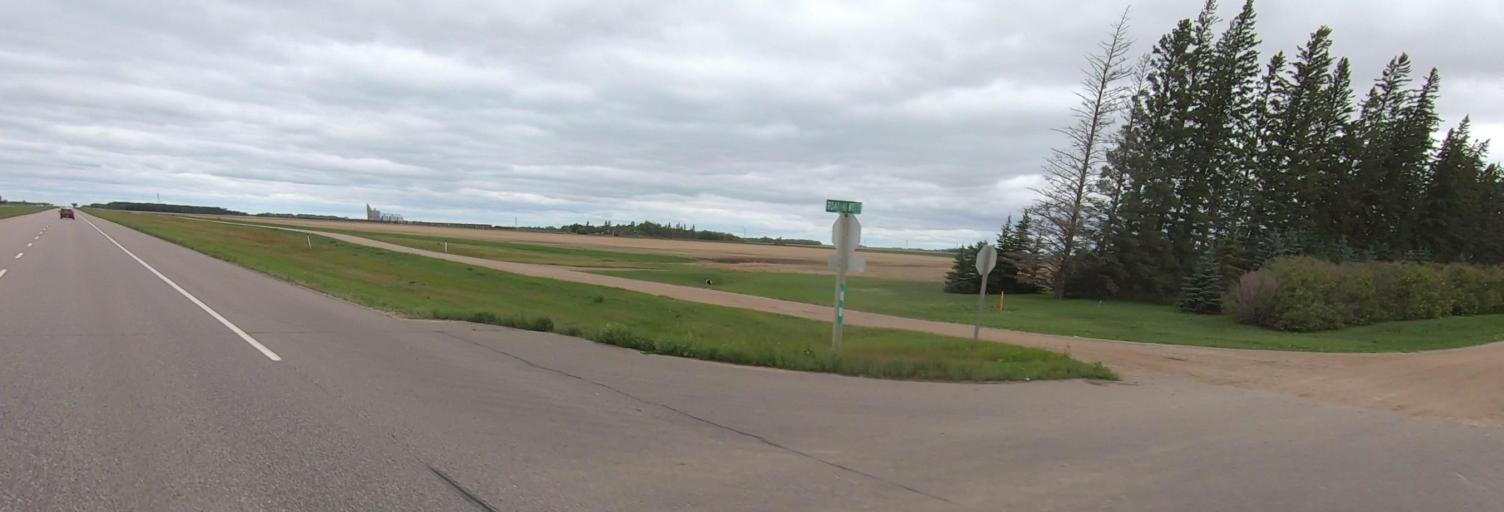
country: CA
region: Manitoba
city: Portage la Prairie
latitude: 49.9752
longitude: -98.5144
